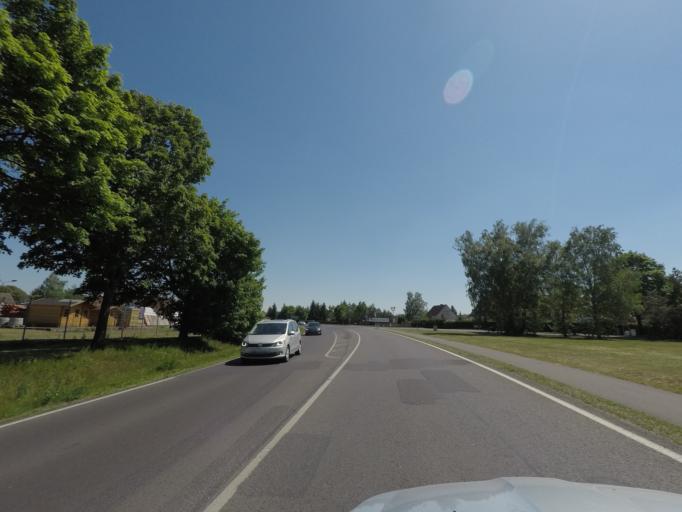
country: DE
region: Brandenburg
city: Melchow
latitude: 52.8435
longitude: 13.6912
